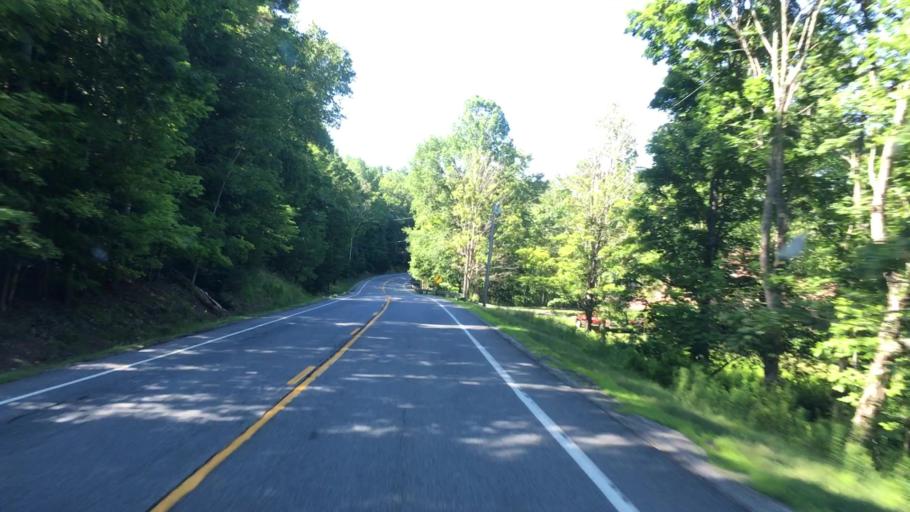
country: US
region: Maine
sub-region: Hancock County
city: Dedham
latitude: 44.6651
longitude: -68.6749
